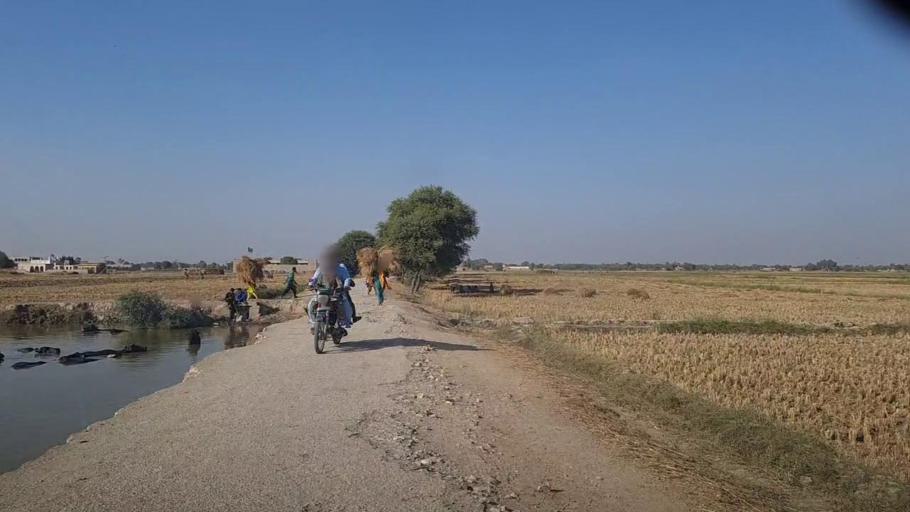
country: PK
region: Sindh
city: Tangwani
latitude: 28.2869
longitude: 68.9846
